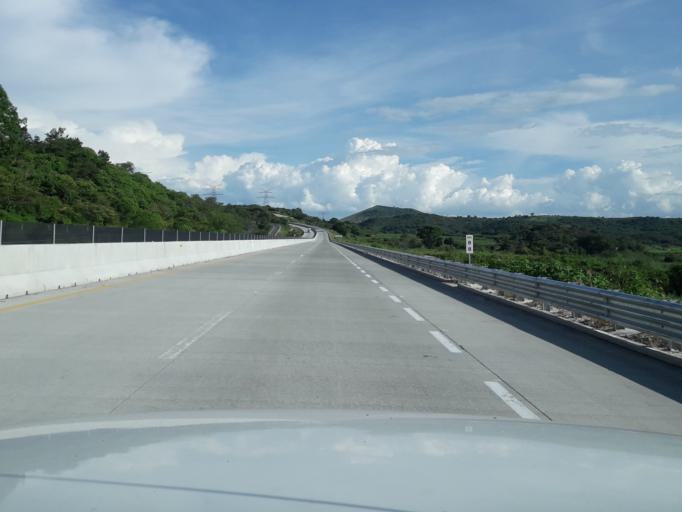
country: MX
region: Jalisco
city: Tala
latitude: 20.5928
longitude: -103.6714
